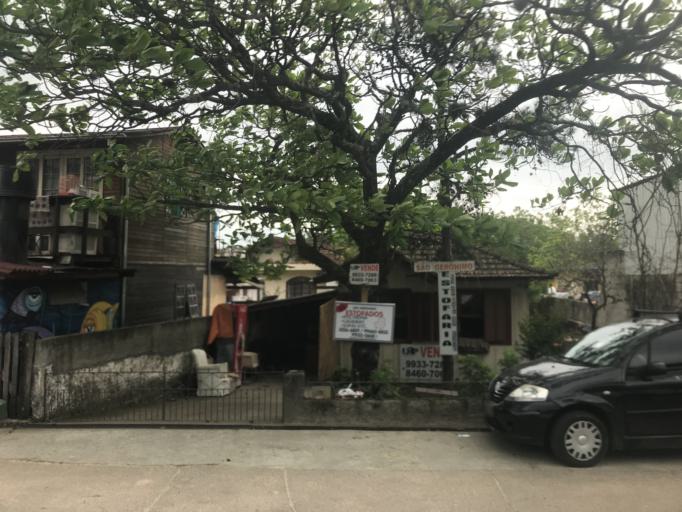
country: BR
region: Santa Catarina
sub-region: Florianopolis
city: Costeira do Pirajubae
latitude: -27.6320
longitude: -48.5237
